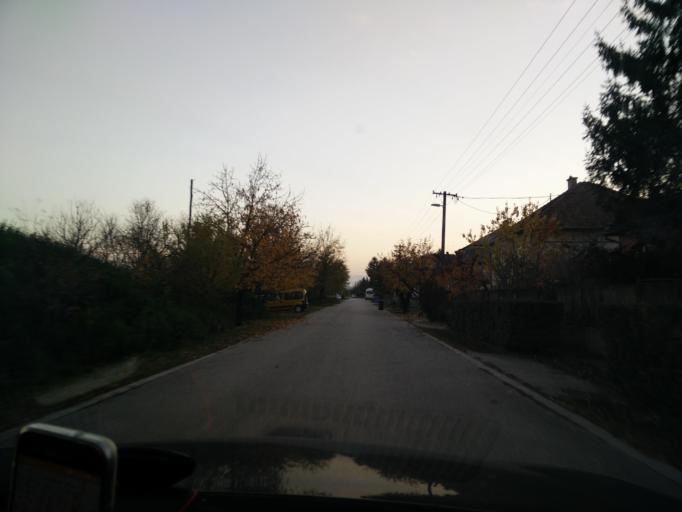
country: HU
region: Komarom-Esztergom
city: Esztergom
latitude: 47.7780
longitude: 18.7422
